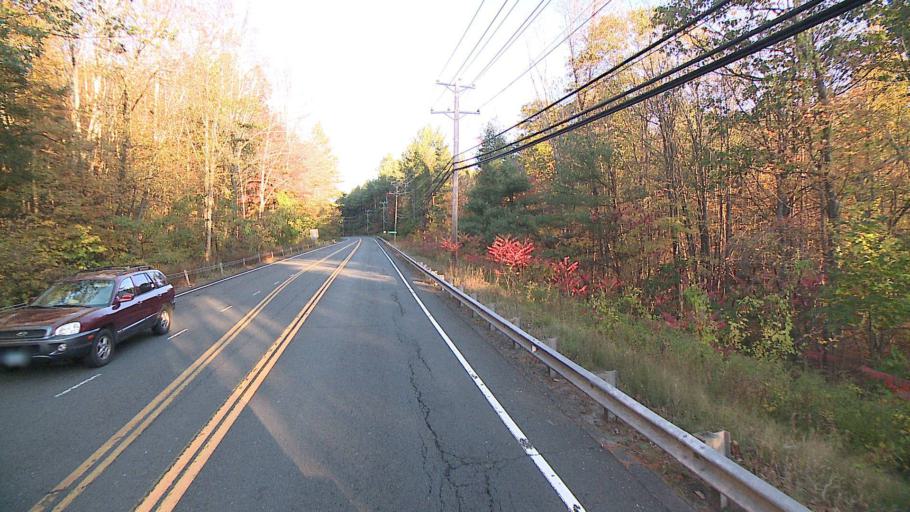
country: US
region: Connecticut
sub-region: Litchfield County
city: New Hartford Center
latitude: 41.9087
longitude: -73.0015
